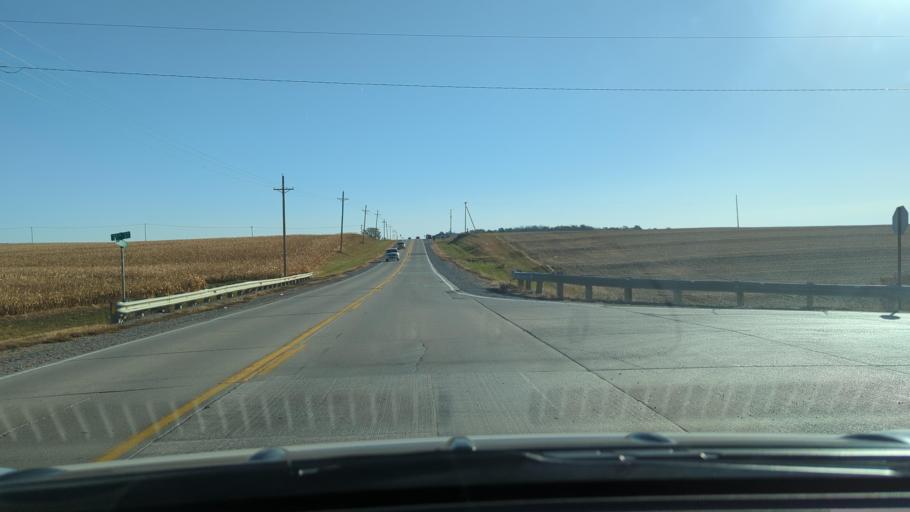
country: US
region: Nebraska
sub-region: Sarpy County
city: Papillion
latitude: 41.0926
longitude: -96.0288
